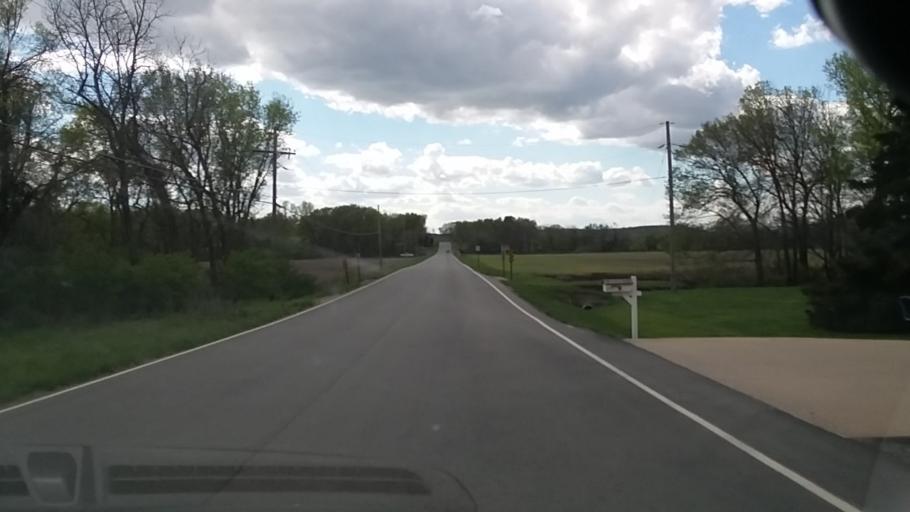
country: US
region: Kansas
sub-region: Douglas County
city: Lawrence
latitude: 38.8991
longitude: -95.2512
